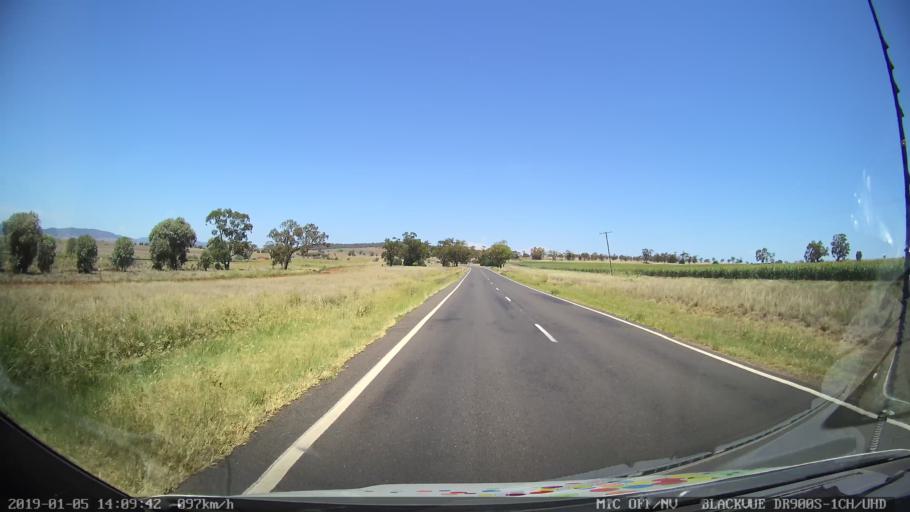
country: AU
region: New South Wales
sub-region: Gunnedah
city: Gunnedah
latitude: -31.2446
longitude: 150.4306
